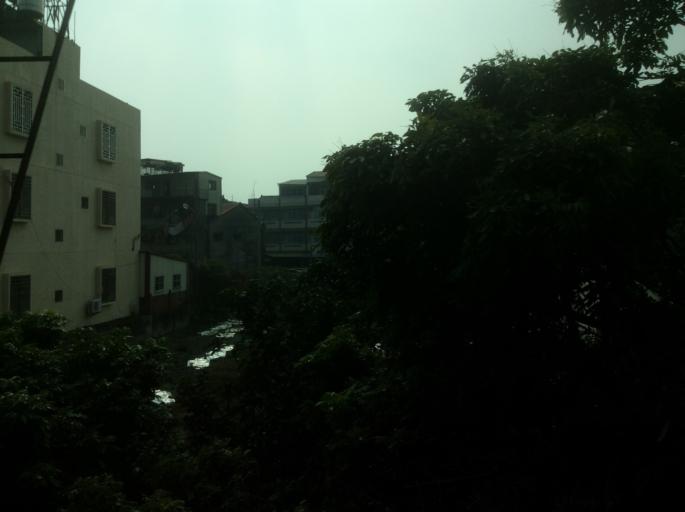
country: TW
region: Taiwan
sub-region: Nantou
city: Nantou
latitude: 23.8156
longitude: 120.6149
